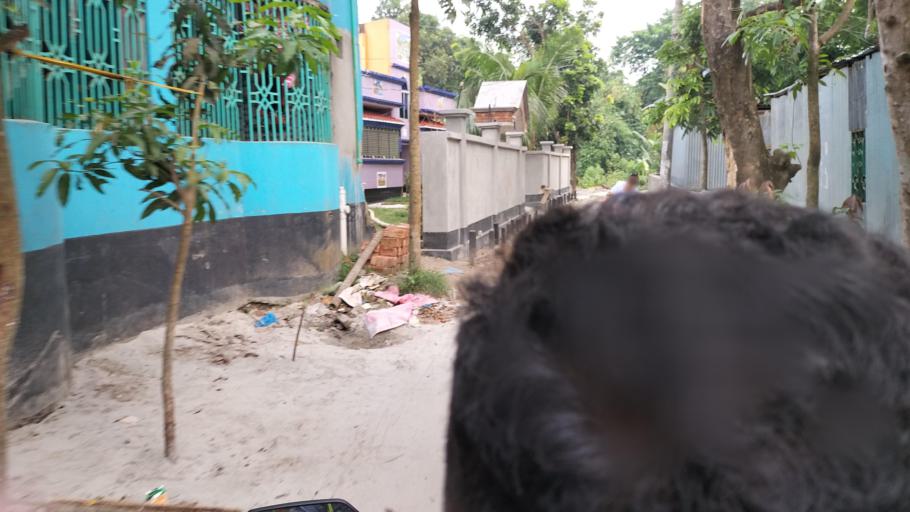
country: BD
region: Dhaka
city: Azimpur
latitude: 23.6798
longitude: 90.3149
